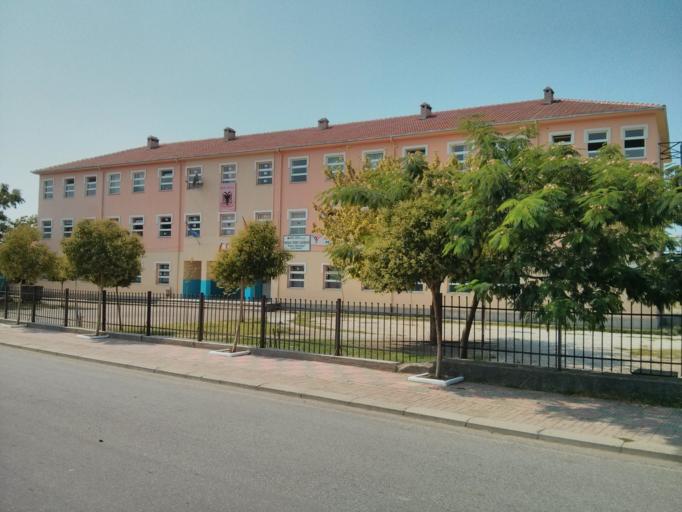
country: AL
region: Shkoder
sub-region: Rrethi i Malesia e Madhe
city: Gruemire
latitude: 42.1157
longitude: 19.5746
